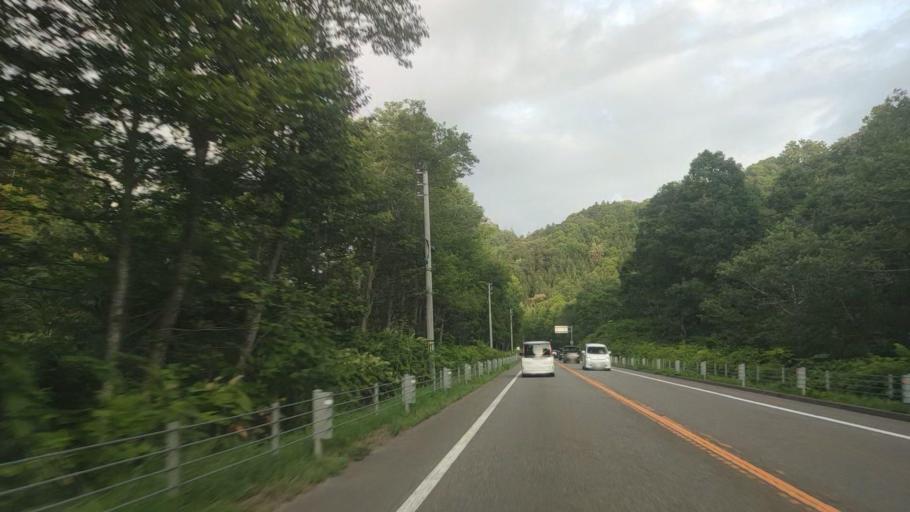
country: JP
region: Hokkaido
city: Utashinai
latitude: 43.2965
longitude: 142.0903
